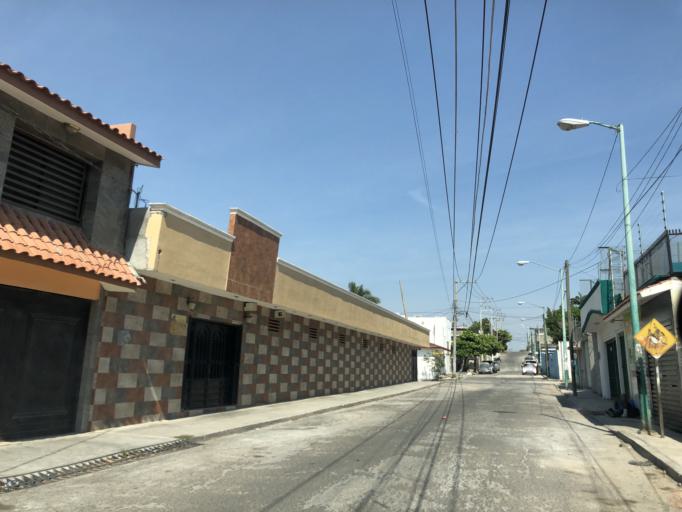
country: MX
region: Chiapas
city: Tuxtla Gutierrez
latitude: 16.7396
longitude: -93.1024
